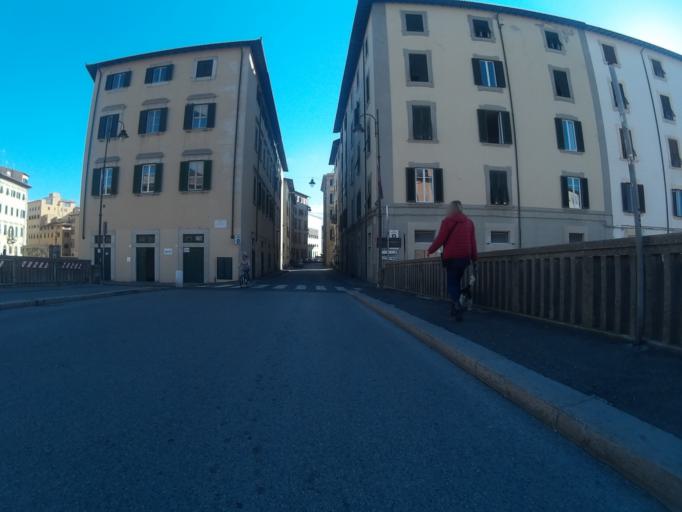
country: IT
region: Tuscany
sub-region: Provincia di Livorno
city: Livorno
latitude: 43.5533
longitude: 10.3065
